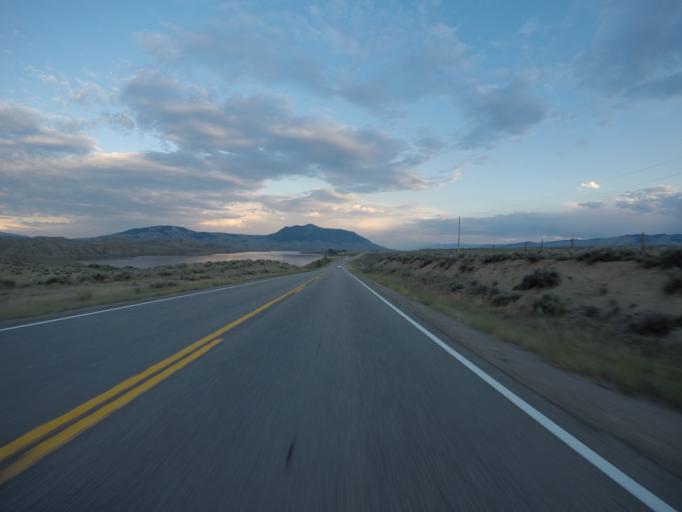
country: US
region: Colorado
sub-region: Grand County
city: Kremmling
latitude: 40.1668
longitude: -106.4167
